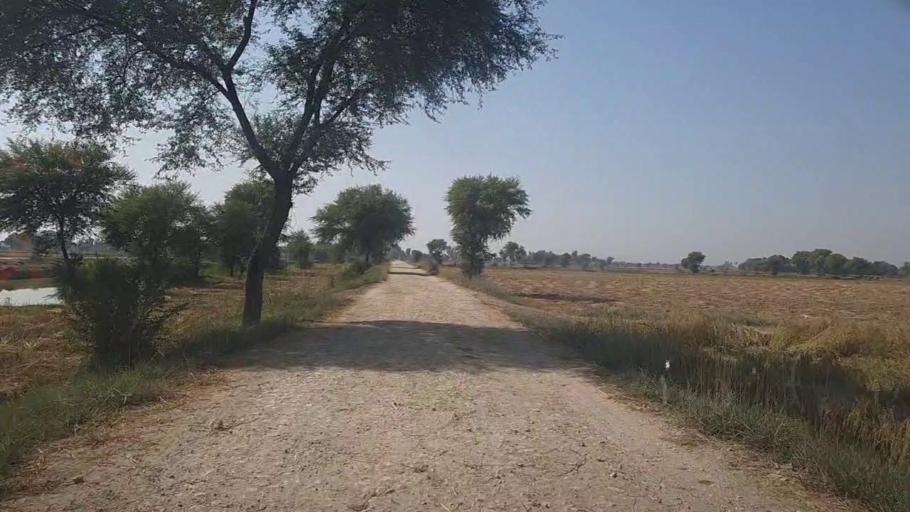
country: PK
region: Sindh
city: Thul
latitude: 28.2510
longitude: 68.8132
